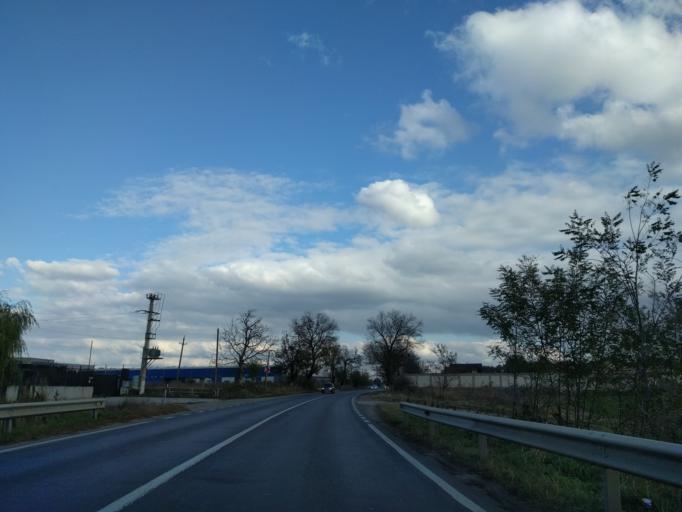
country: RO
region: Ilfov
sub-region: Comuna Ganeasa
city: Ganeasa
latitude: 44.4559
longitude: 26.2764
